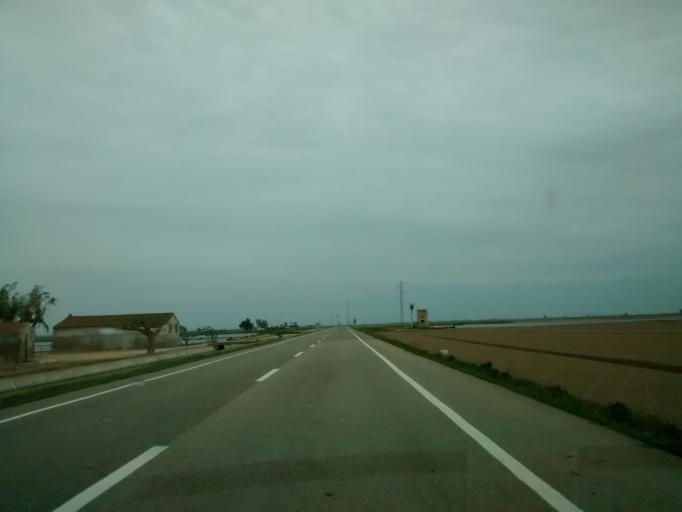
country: ES
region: Catalonia
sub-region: Provincia de Tarragona
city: Deltebre
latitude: 40.6964
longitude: 0.6799
